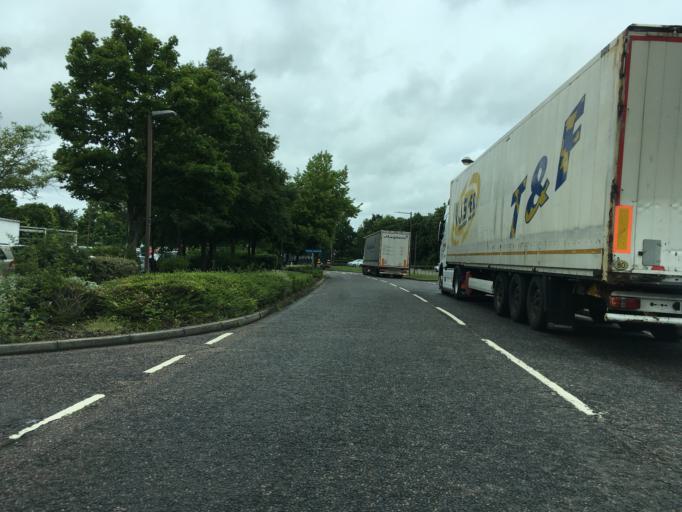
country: GB
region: England
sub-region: Milton Keynes
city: Broughton
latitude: 52.0362
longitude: -0.6860
